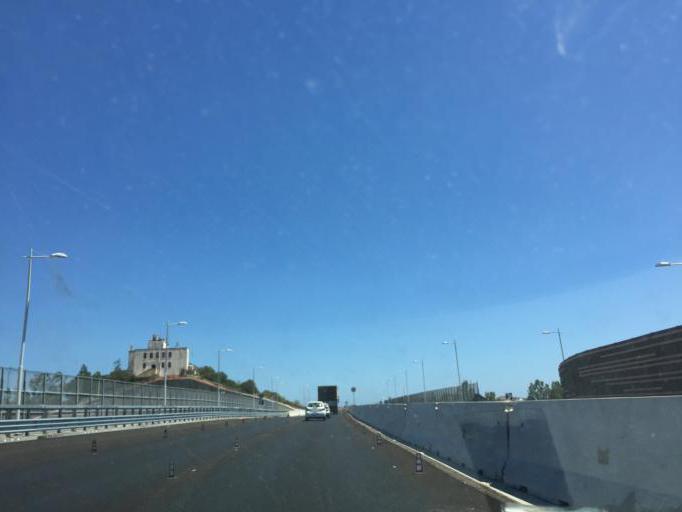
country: IT
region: Sardinia
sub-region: Provincia di Olbia-Tempio
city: Olbia
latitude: 40.9049
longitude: 9.5008
